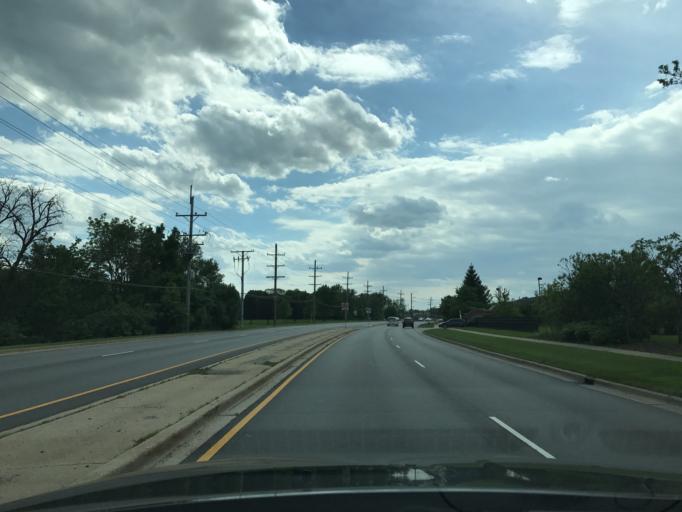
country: US
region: Illinois
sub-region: DuPage County
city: Lisle
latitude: 41.7833
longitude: -88.0886
